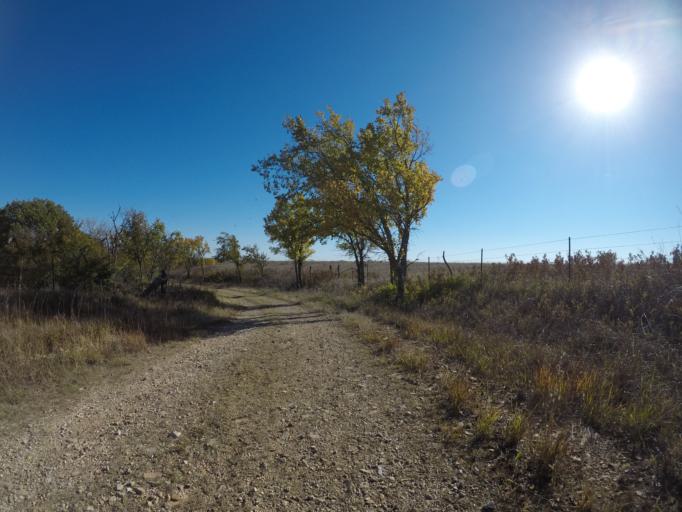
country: US
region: Kansas
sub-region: Wabaunsee County
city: Alma
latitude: 38.8878
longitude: -96.3936
